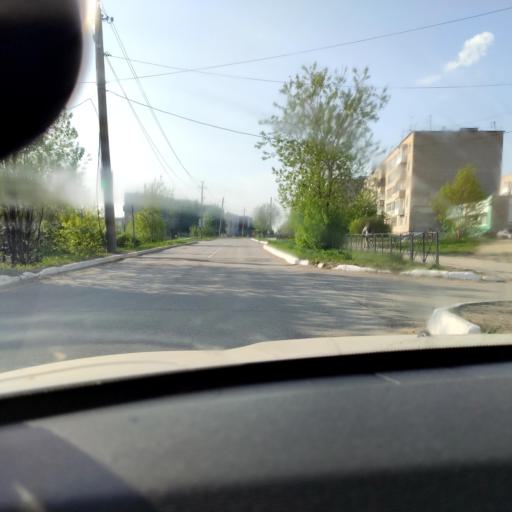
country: RU
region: Perm
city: Polazna
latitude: 58.2928
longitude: 56.3949
